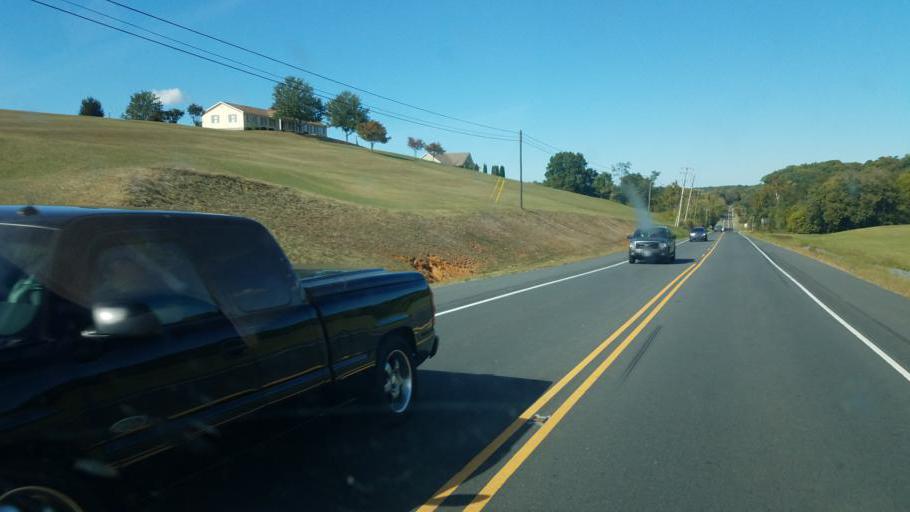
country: US
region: Virginia
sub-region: Warren County
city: Front Royal
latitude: 38.8764
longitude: -78.2467
